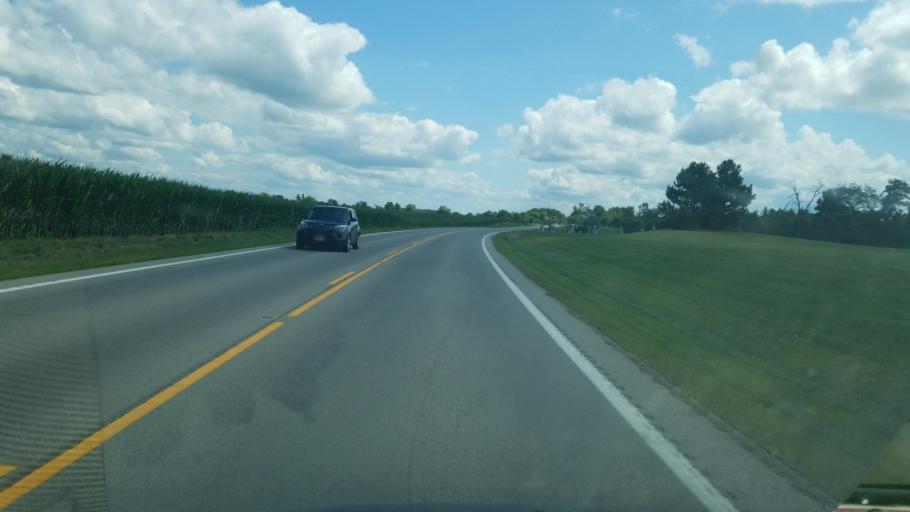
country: US
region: Ohio
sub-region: Putnam County
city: Kalida
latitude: 40.9470
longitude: -84.1626
